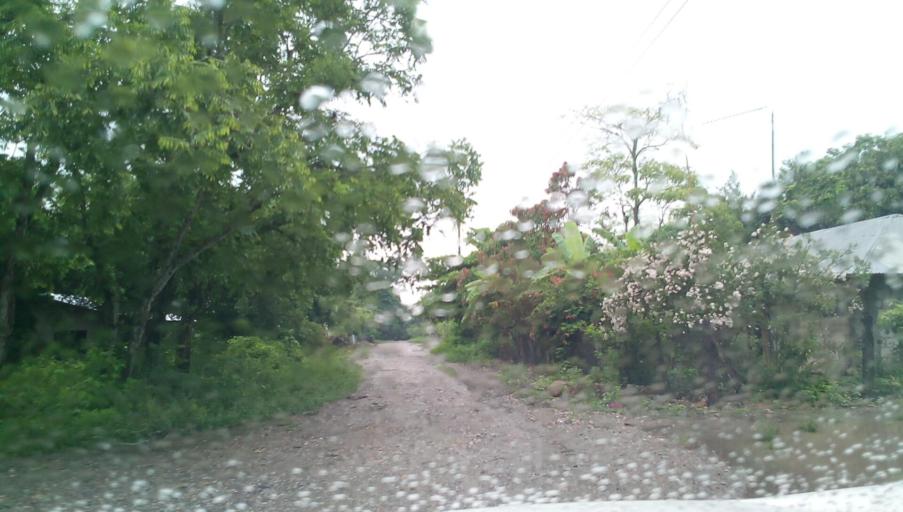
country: MX
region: Veracruz
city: Tempoal de Sanchez
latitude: 21.4152
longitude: -98.4251
